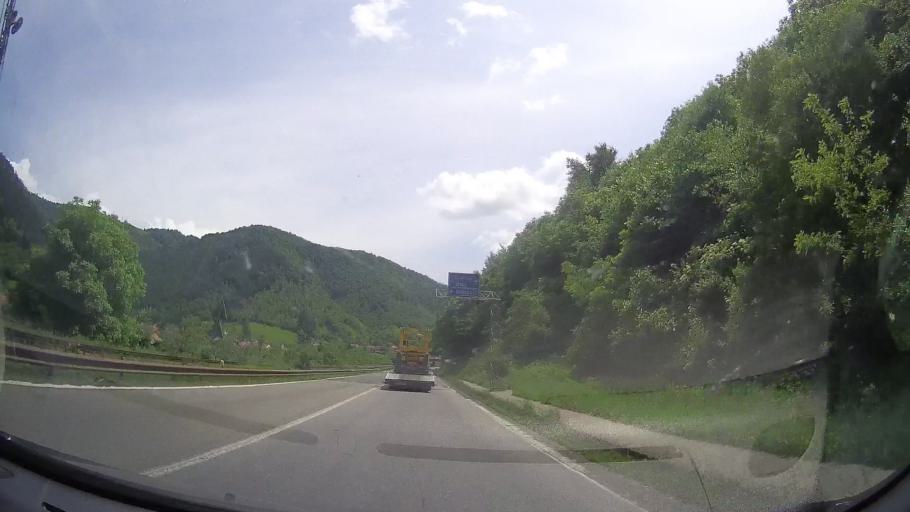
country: RO
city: Cainenii Mici
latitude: 45.4986
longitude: 24.3020
